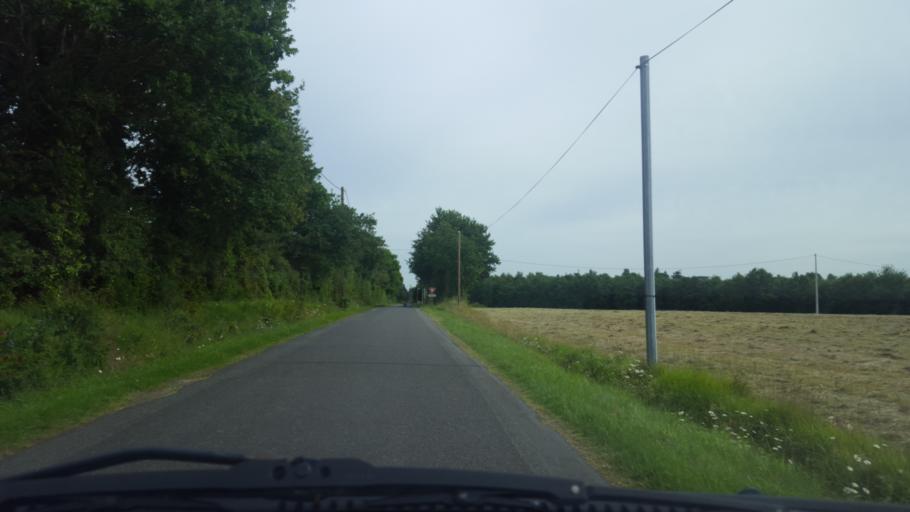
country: FR
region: Pays de la Loire
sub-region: Departement de la Loire-Atlantique
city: La Limouziniere
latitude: 46.9936
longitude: -1.5875
